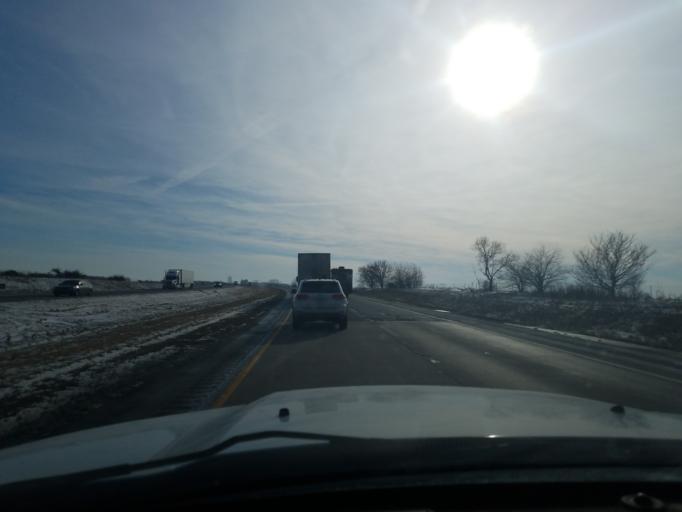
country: US
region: Indiana
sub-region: Huntington County
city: Markle
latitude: 40.7987
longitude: -85.3833
